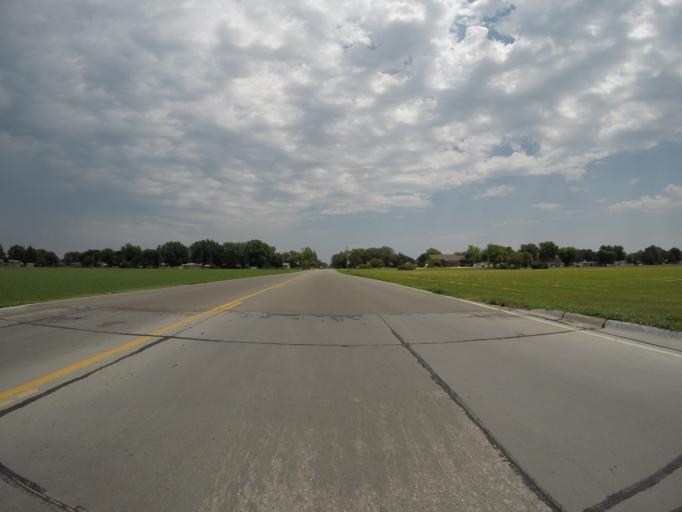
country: US
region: Nebraska
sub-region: Adams County
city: Hastings
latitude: 40.5970
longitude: -98.4204
